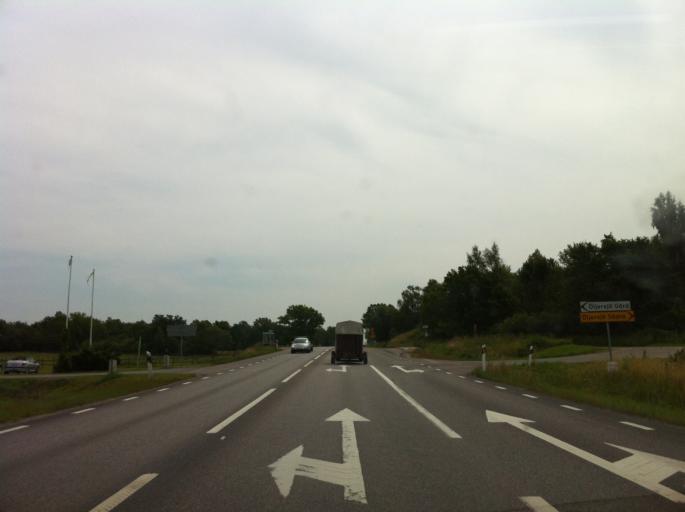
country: SE
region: Blekinge
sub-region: Karlskrona Kommun
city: Sturko
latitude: 56.1885
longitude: 15.7109
